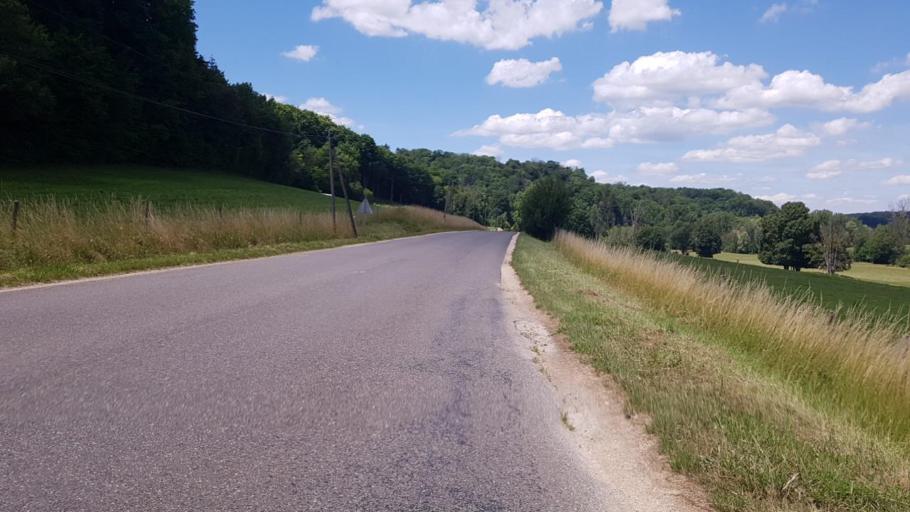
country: FR
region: Lorraine
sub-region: Departement de la Meuse
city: Gondrecourt-le-Chateau
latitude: 48.6316
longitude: 5.4600
